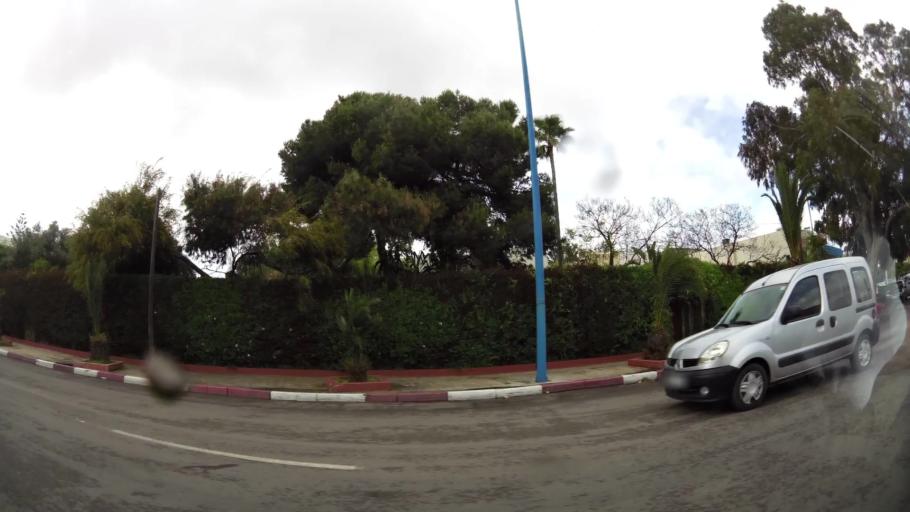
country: MA
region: Grand Casablanca
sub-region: Casablanca
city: Casablanca
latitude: 33.5513
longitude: -7.6109
